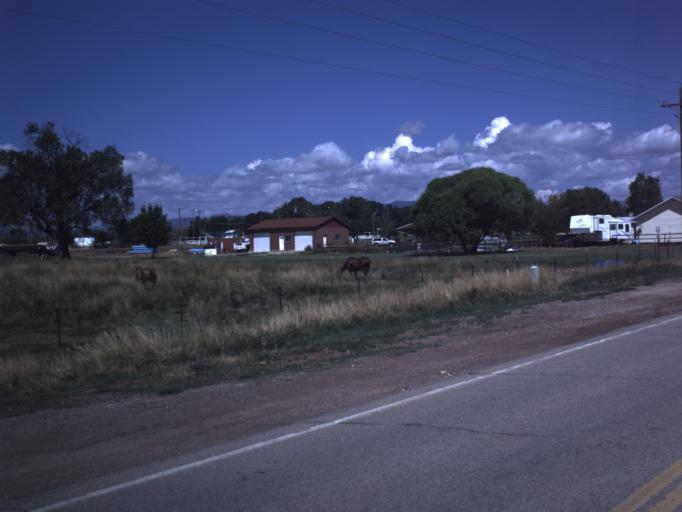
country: US
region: Utah
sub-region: Duchesne County
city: Roosevelt
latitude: 40.4277
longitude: -110.0300
